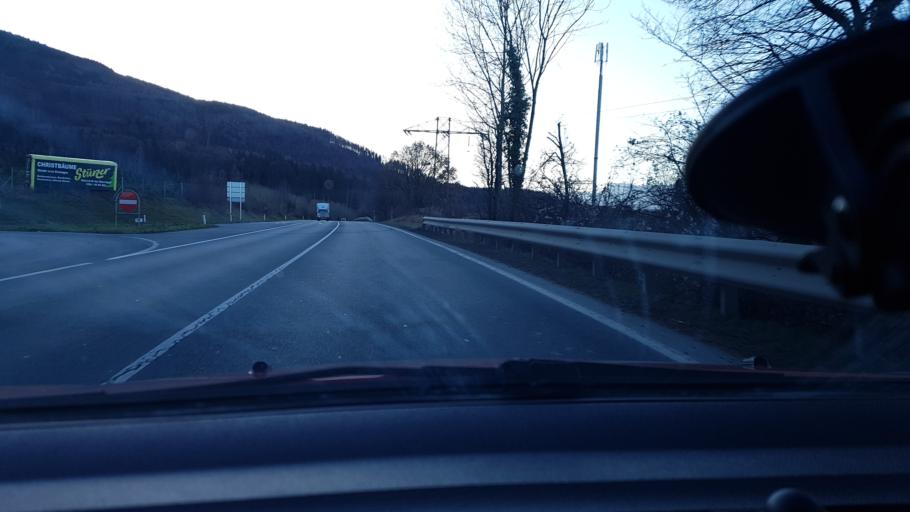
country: DE
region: Bavaria
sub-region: Upper Bavaria
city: Laufen
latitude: 47.9250
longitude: 12.9705
